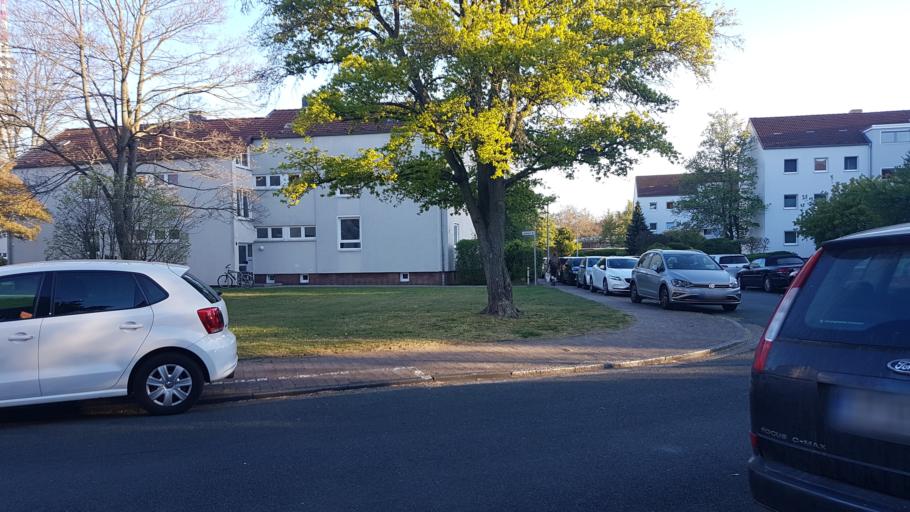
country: DE
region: Lower Saxony
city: Hannover
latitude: 52.3992
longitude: 9.7944
